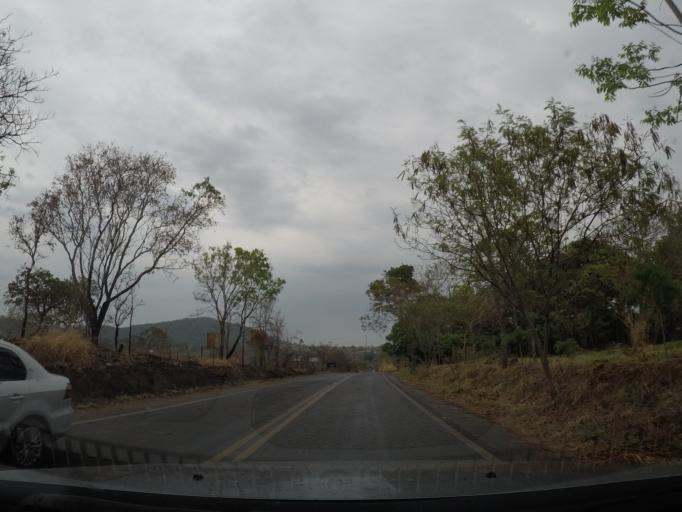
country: BR
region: Goias
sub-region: Pirenopolis
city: Pirenopolis
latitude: -15.8517
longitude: -48.9340
